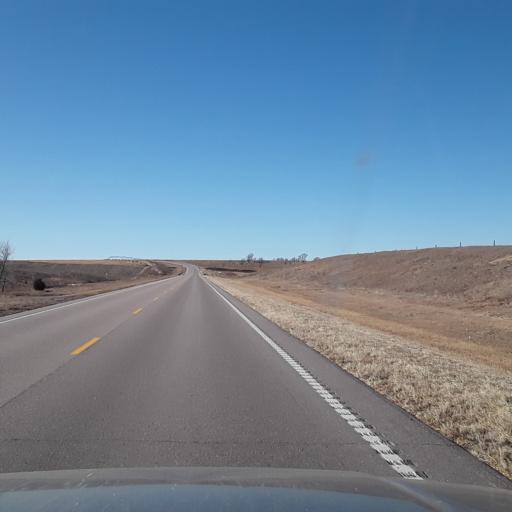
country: US
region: Nebraska
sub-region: Frontier County
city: Stockville
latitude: 40.7057
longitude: -100.2351
